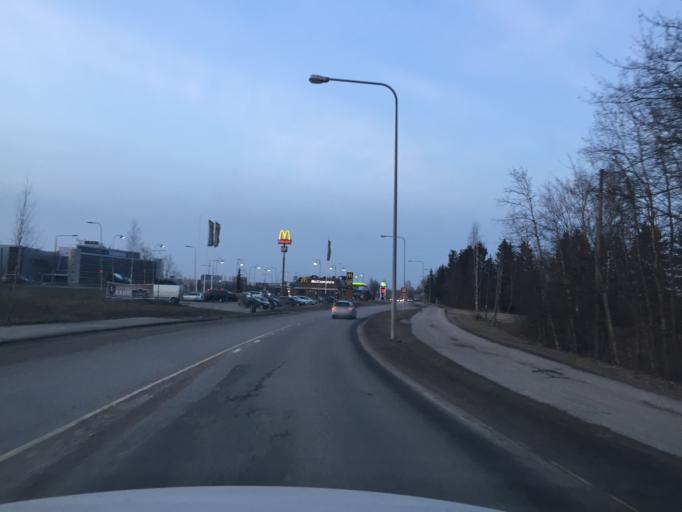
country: FI
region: Uusimaa
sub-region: Helsinki
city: Vantaa
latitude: 60.2694
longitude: 24.9745
